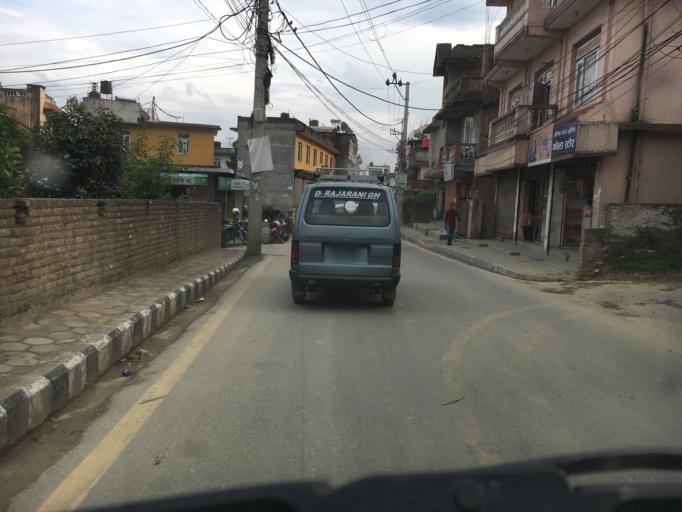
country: NP
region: Central Region
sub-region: Bagmati Zone
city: Kathmandu
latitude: 27.7377
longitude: 85.3486
